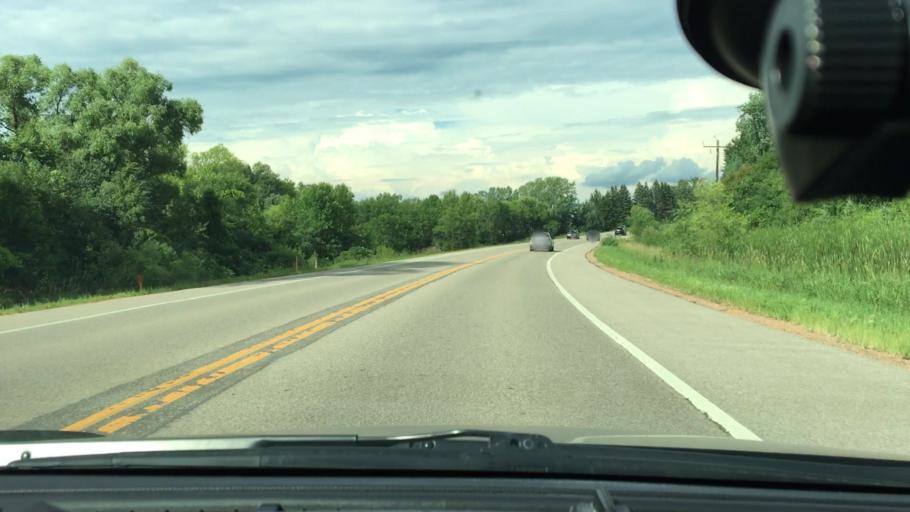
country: US
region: Minnesota
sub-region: Carver County
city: Victoria
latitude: 44.8654
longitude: -93.6511
